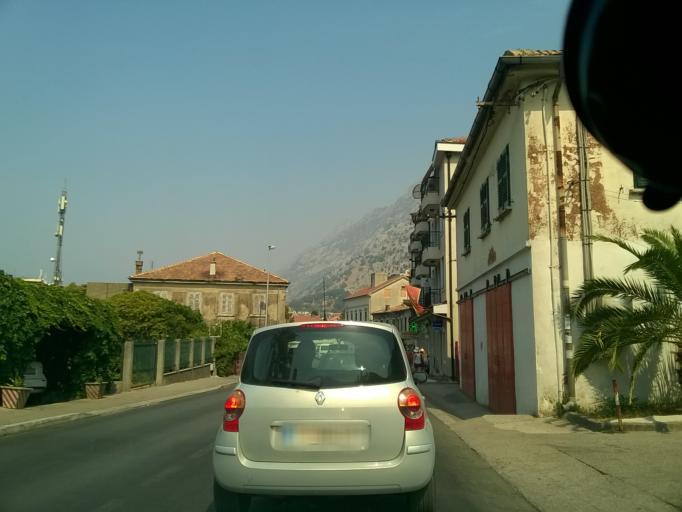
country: ME
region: Kotor
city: Kotor
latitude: 42.4205
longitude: 18.7699
